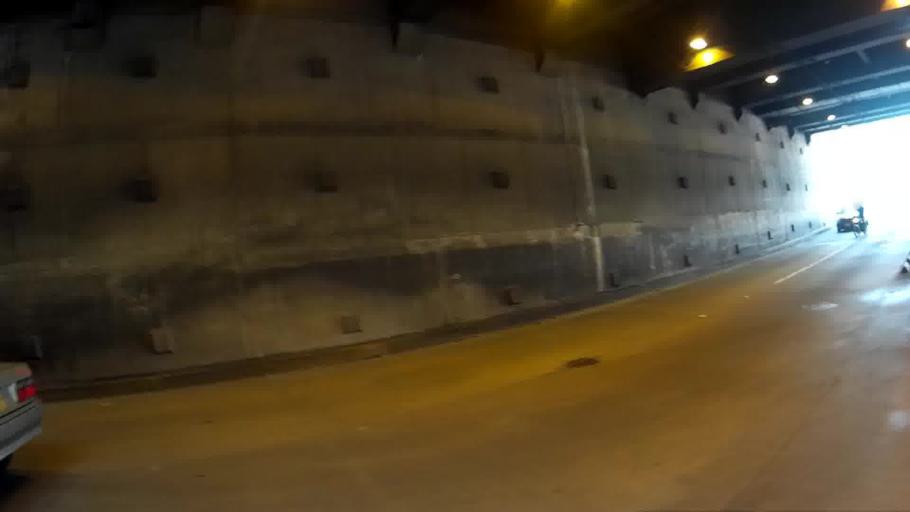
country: CO
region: Risaralda
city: Pereira
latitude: 4.8051
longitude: -75.7385
